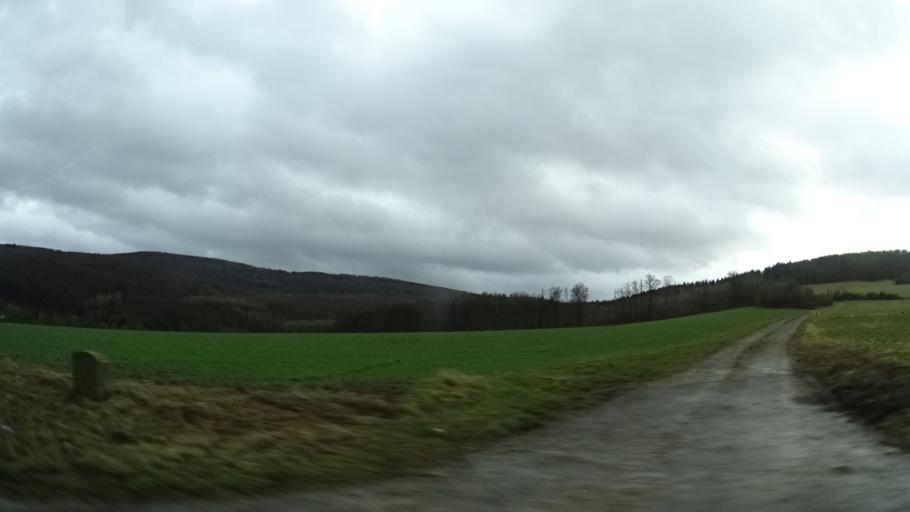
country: DE
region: Thuringia
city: Unterkatz
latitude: 50.6064
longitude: 10.2469
